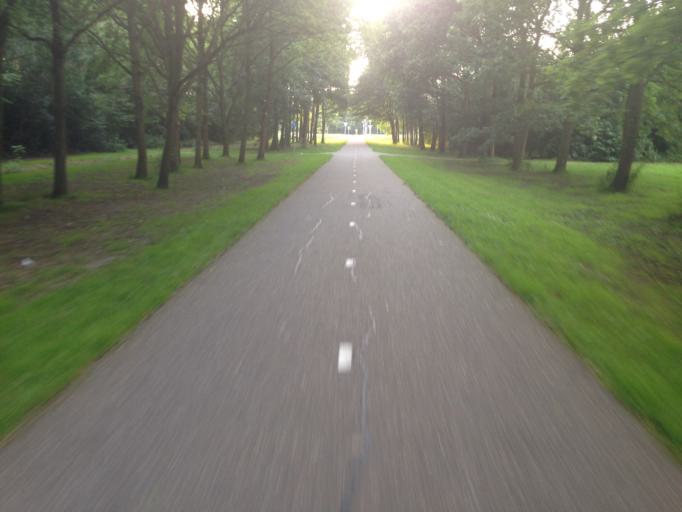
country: NL
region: Flevoland
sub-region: Gemeente Almere
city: Almere Stad
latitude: 52.3940
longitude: 5.2888
